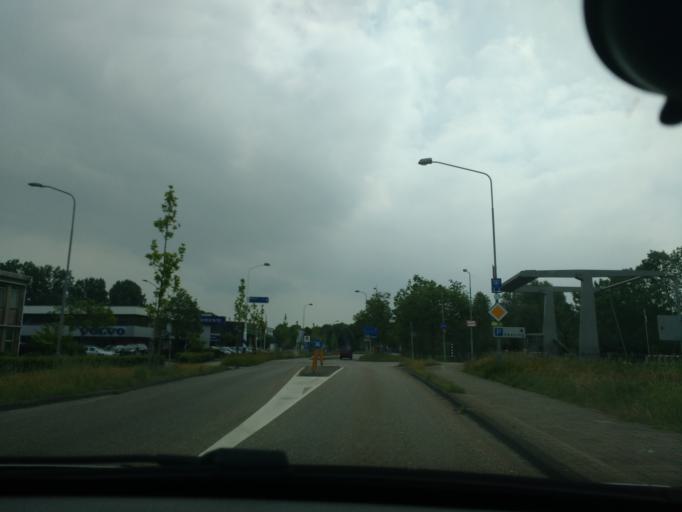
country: NL
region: North Holland
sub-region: Gemeente Naarden
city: Naarden
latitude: 52.2996
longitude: 5.1543
